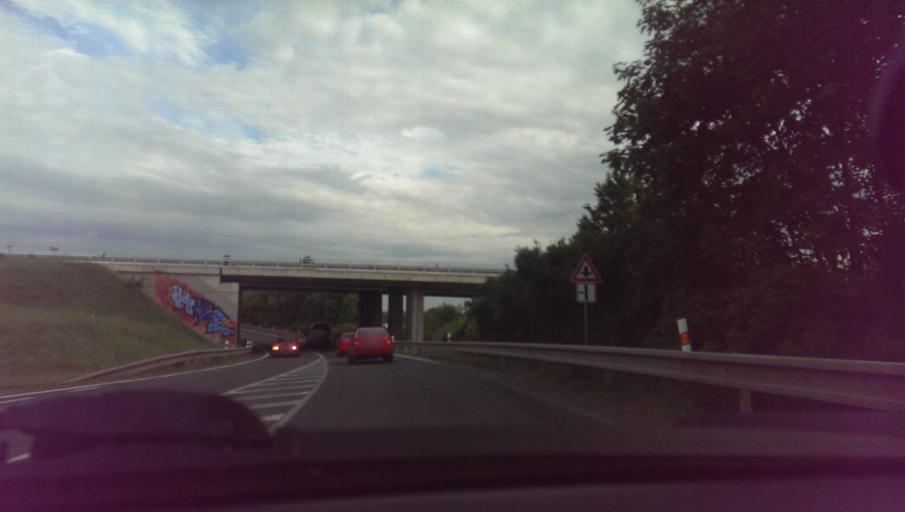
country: CZ
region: Zlin
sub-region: Okres Kromeriz
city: Kromeriz
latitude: 49.3108
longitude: 17.3774
